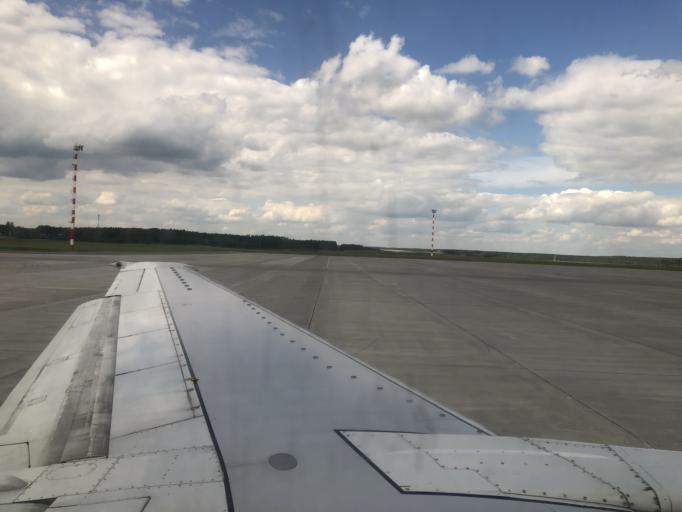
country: BY
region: Minsk
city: Horad Smalyavichy
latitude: 53.8903
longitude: 28.0461
